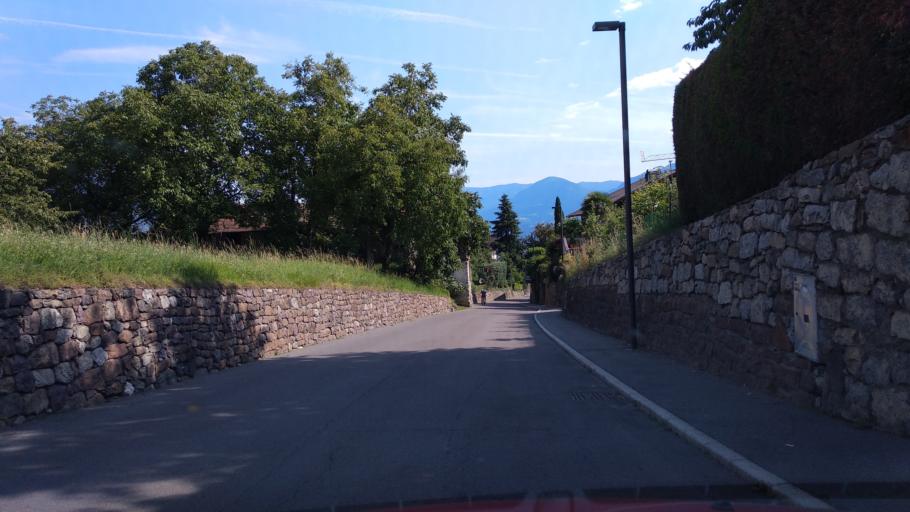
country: IT
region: Trentino-Alto Adige
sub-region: Bolzano
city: Tirolo
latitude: 46.6955
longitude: 11.1543
